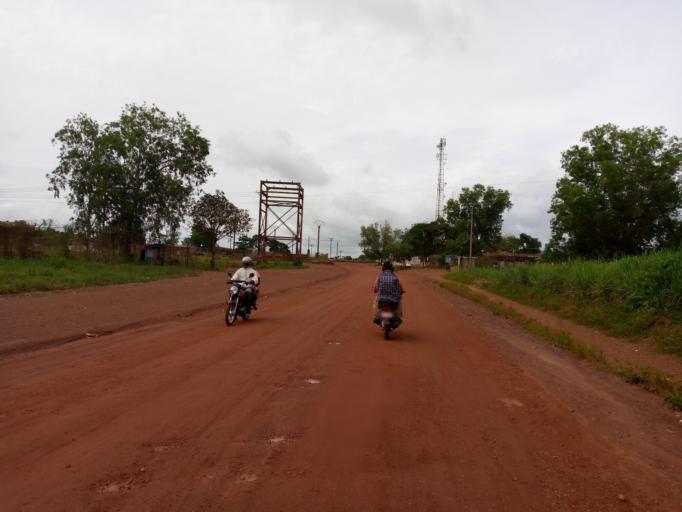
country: SL
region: Southern Province
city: Mogbwemo
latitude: 7.7676
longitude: -12.2960
